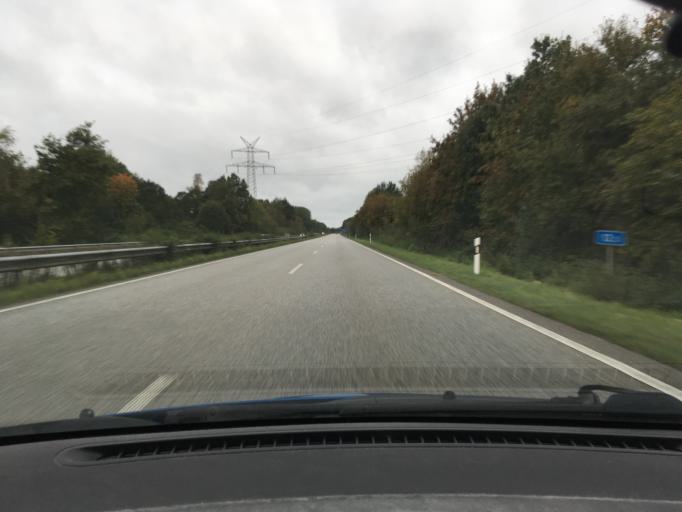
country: DE
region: Schleswig-Holstein
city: Bredenbek
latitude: 54.3143
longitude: 9.8832
